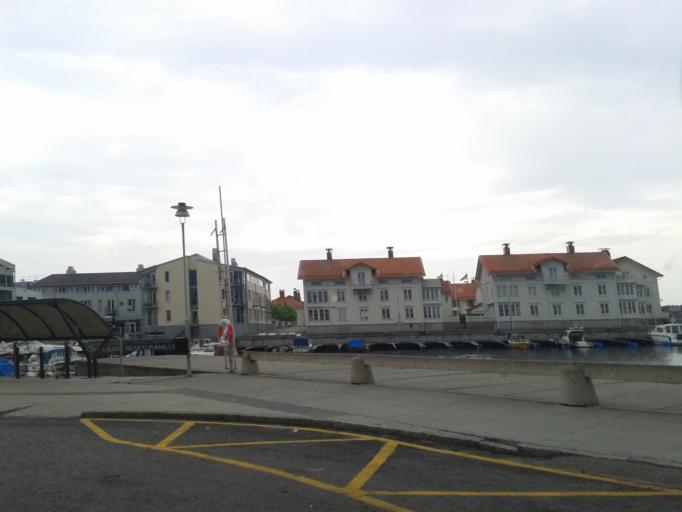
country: SE
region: Vaestra Goetaland
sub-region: Kungalvs Kommun
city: Marstrand
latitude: 57.8867
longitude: 11.5886
